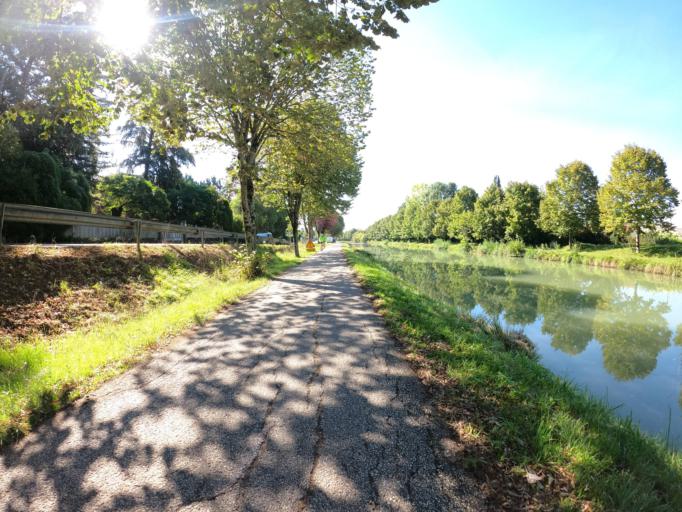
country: FR
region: Aquitaine
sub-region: Departement du Lot-et-Garonne
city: Agen
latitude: 44.2037
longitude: 0.6431
